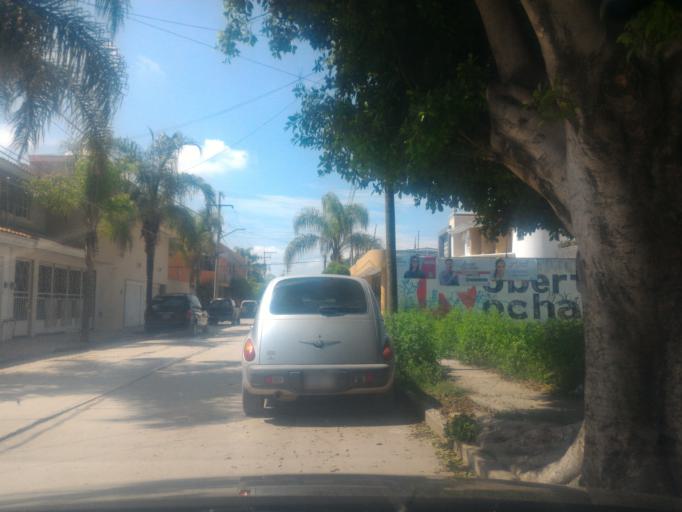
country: MX
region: Guanajuato
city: San Francisco del Rincon
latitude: 21.0109
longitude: -101.8633
